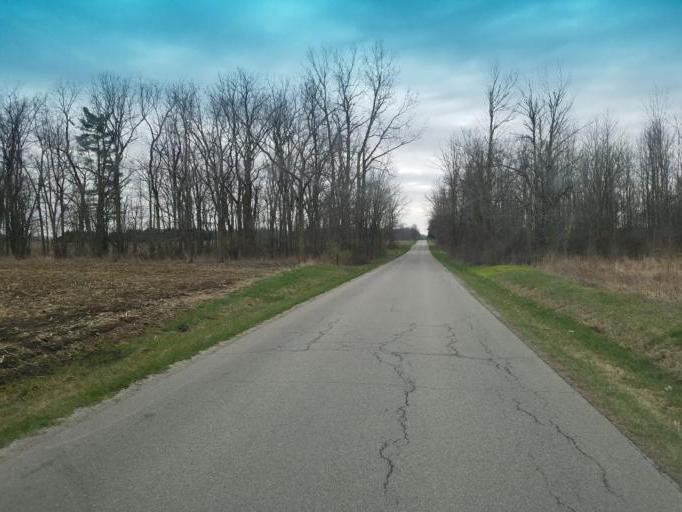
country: US
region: Ohio
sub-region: Crawford County
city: Bucyrus
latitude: 40.8348
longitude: -82.9306
